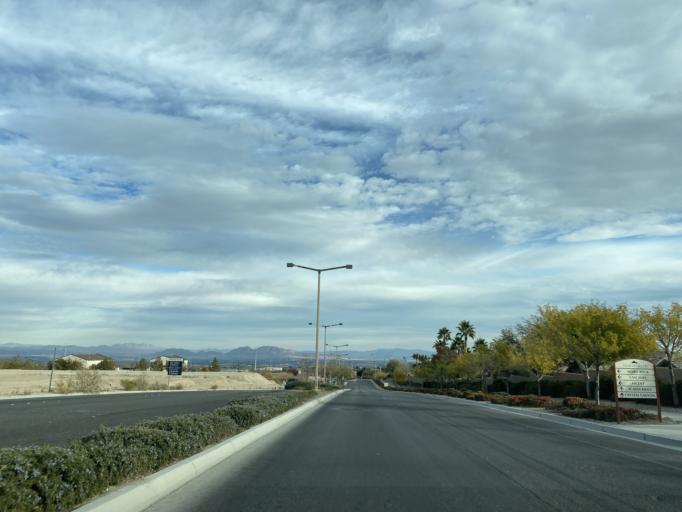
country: US
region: Nevada
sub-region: Clark County
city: Summerlin South
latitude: 36.1814
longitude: -115.3523
